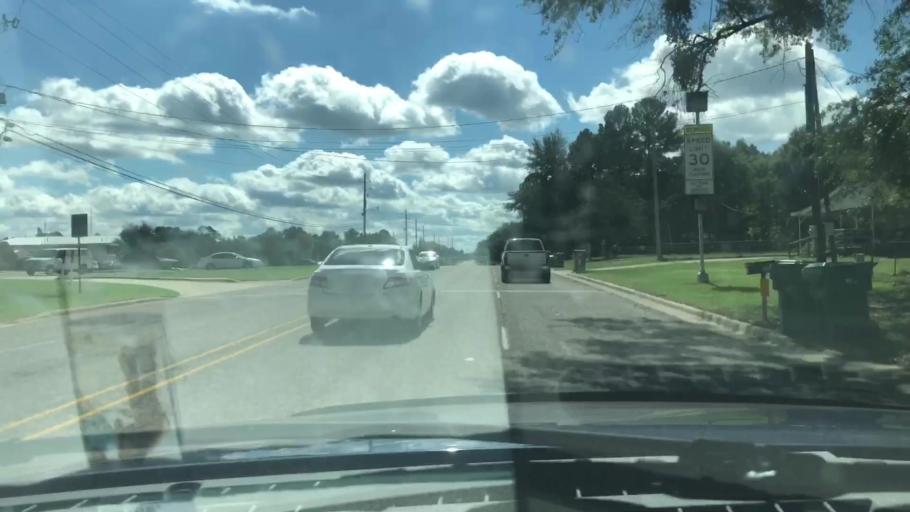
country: US
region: Texas
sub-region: Bowie County
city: Wake Village
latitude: 33.3933
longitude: -94.0922
